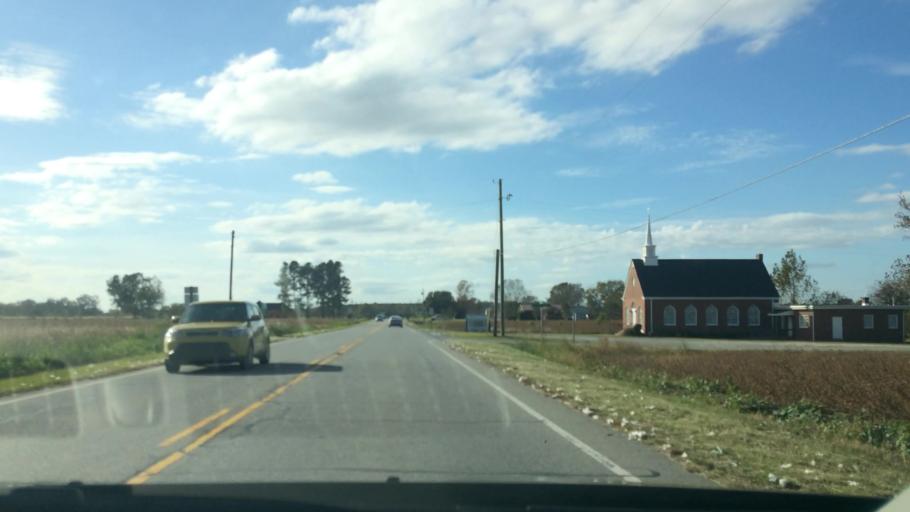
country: US
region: North Carolina
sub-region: Greene County
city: Snow Hill
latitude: 35.4404
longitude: -77.8045
